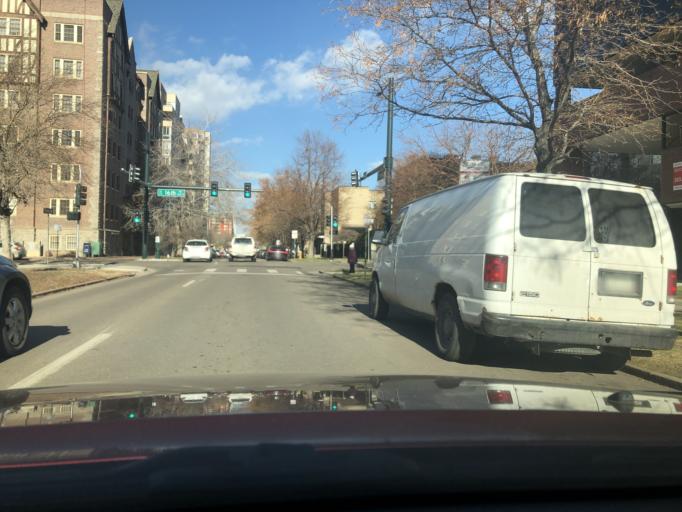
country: US
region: Colorado
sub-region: Denver County
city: Denver
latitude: 39.7413
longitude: -104.9823
